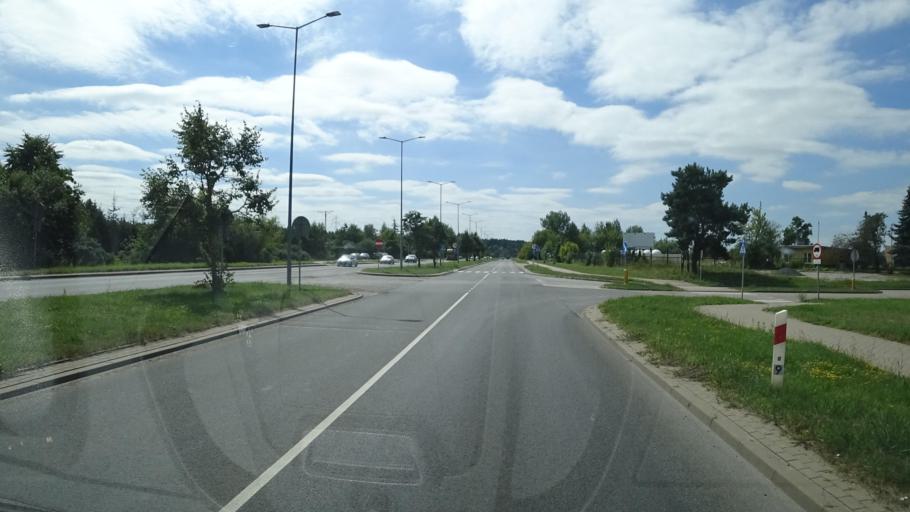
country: PL
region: Warmian-Masurian Voivodeship
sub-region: Powiat elcki
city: Elk
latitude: 53.8263
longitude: 22.3911
